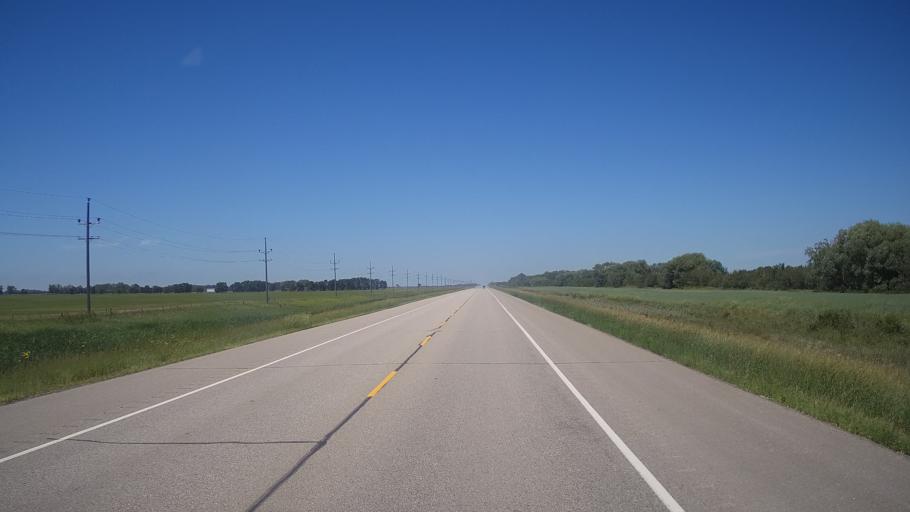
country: CA
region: Manitoba
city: Neepawa
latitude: 50.2257
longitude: -99.0428
